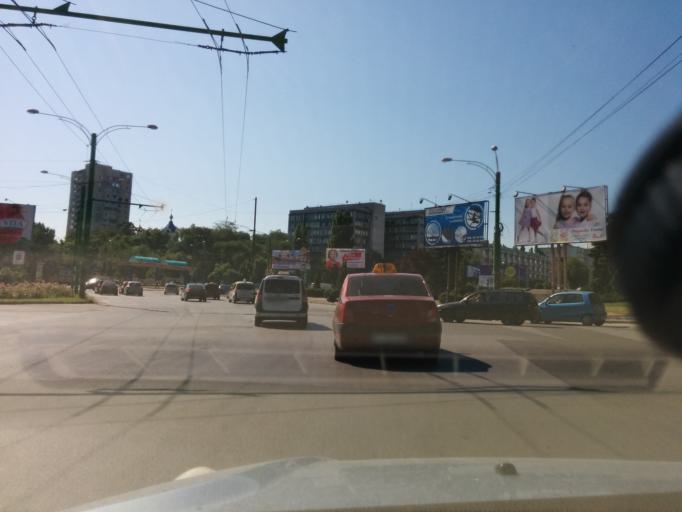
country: MD
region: Chisinau
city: Chisinau
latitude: 47.0115
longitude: 28.8576
